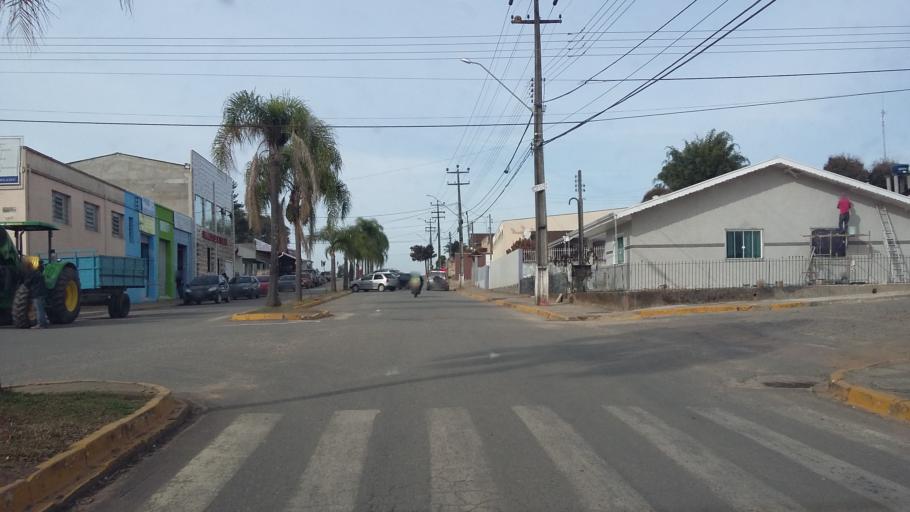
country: BR
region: Parana
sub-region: Lapa
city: Lapa
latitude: -25.8716
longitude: -49.4990
